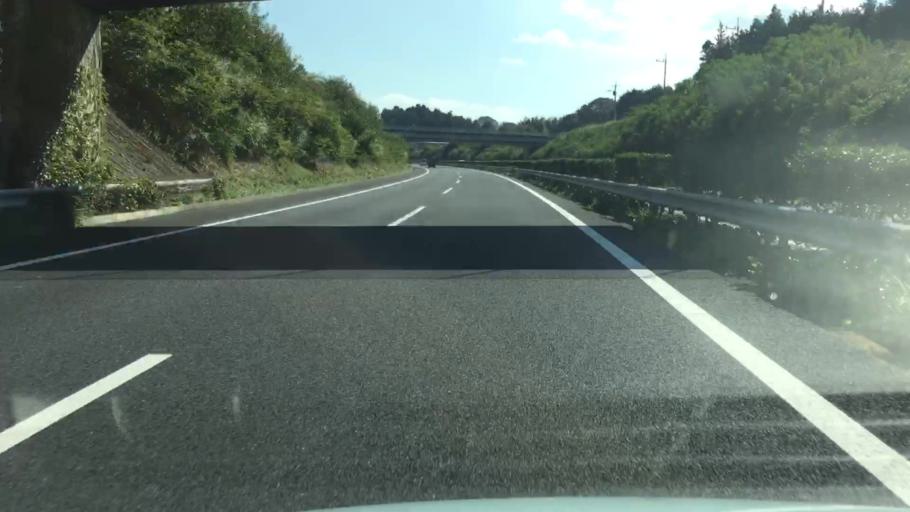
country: JP
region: Ibaraki
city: Tomobe
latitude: 36.3162
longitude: 140.3158
